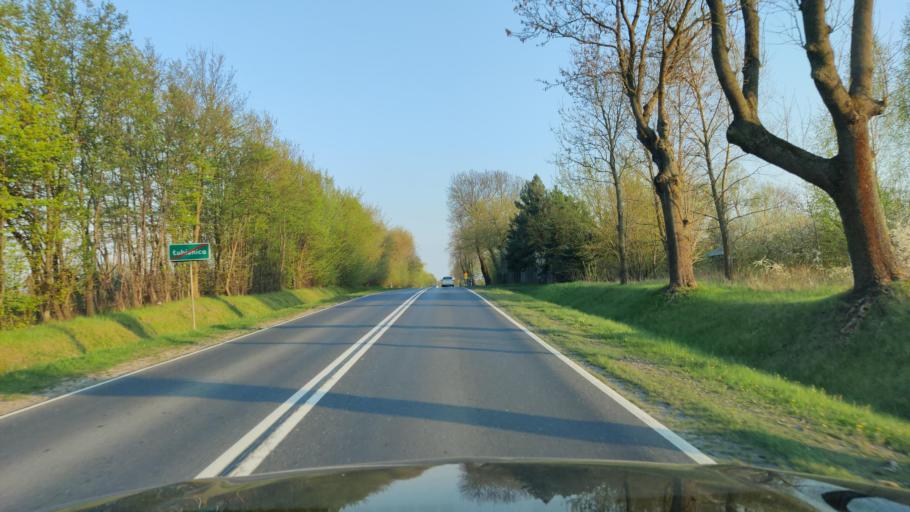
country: PL
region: Masovian Voivodeship
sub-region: Powiat pultuski
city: Pultusk
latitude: 52.6474
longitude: 21.0896
